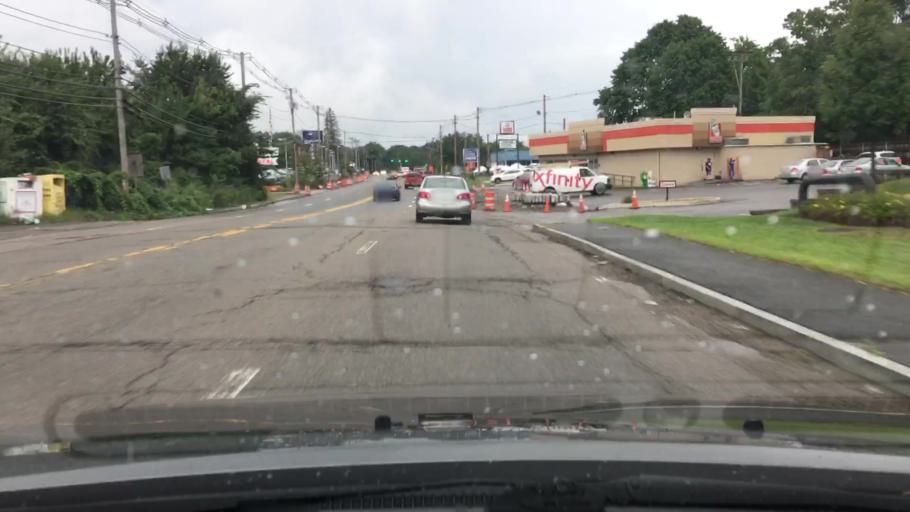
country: US
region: Massachusetts
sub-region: Norfolk County
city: Plainville
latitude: 41.9630
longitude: -71.3403
